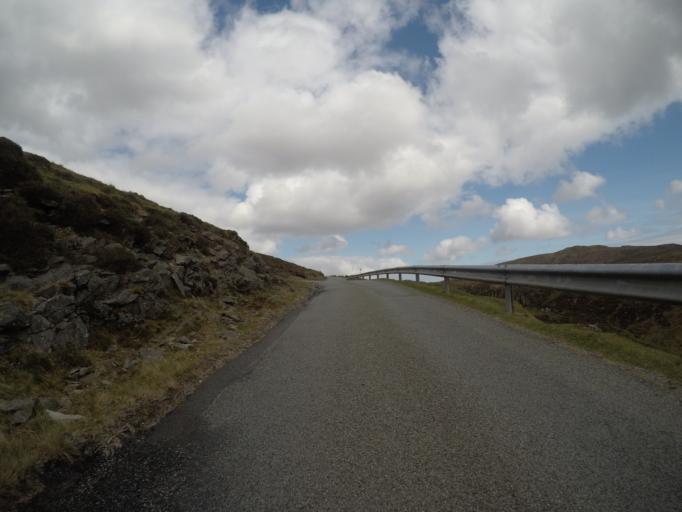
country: GB
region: Scotland
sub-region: Highland
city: Isle of Skye
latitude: 57.3787
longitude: -6.3659
